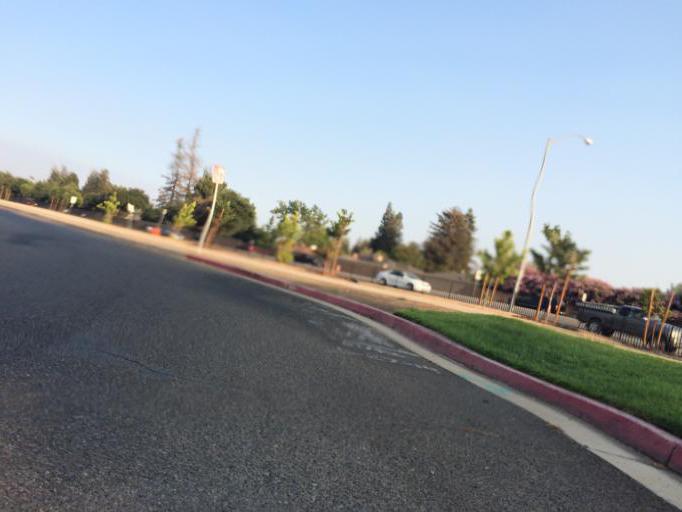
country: US
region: California
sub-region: Fresno County
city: Fresno
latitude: 36.8373
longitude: -119.8165
